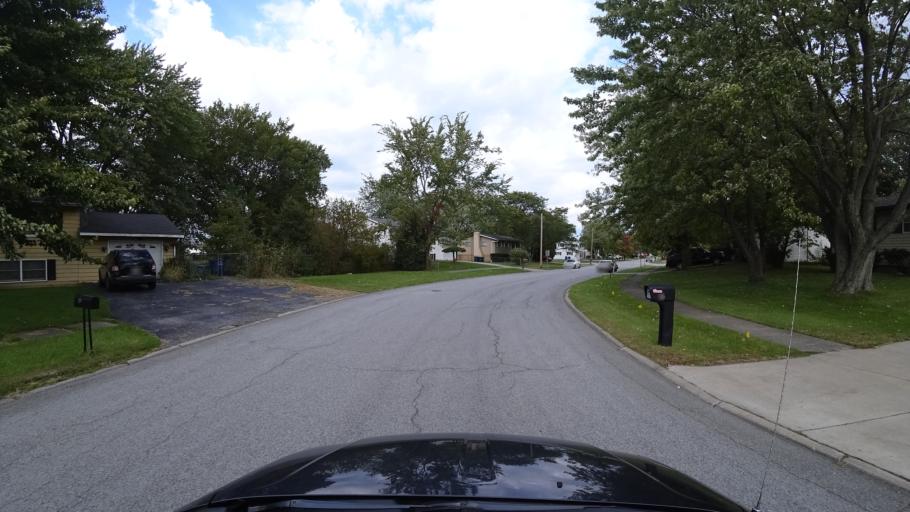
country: US
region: Indiana
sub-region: LaPorte County
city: Michigan City
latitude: 41.6738
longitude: -86.9024
